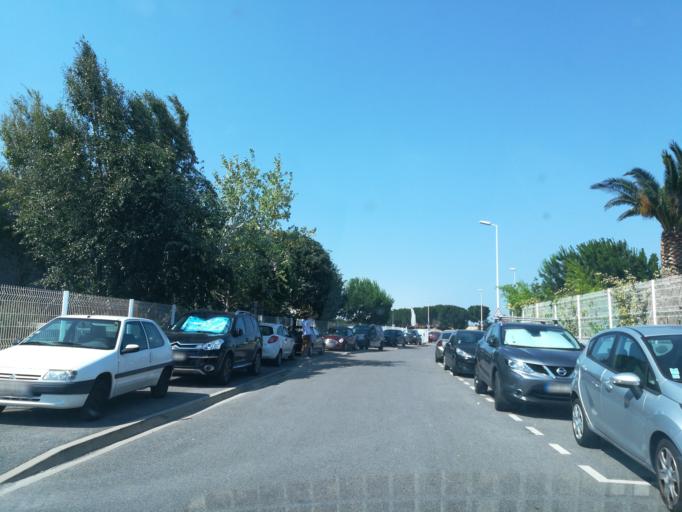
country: FR
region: Languedoc-Roussillon
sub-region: Departement des Pyrenees-Orientales
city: Pia
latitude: 42.7322
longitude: 2.8861
